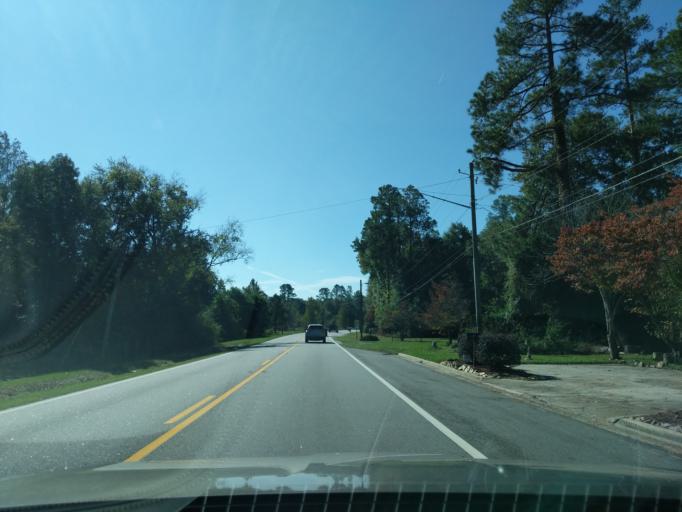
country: US
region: Georgia
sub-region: Richmond County
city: Hephzibah
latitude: 33.3589
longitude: -81.9974
